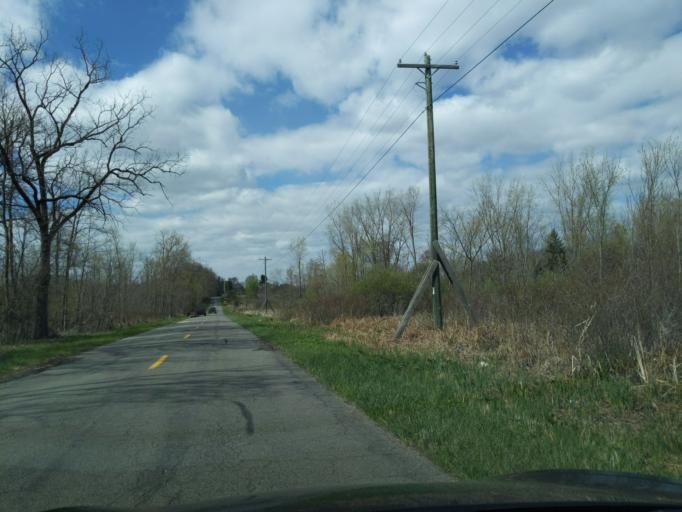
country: US
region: Michigan
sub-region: Ingham County
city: Leslie
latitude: 42.4320
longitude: -84.5409
